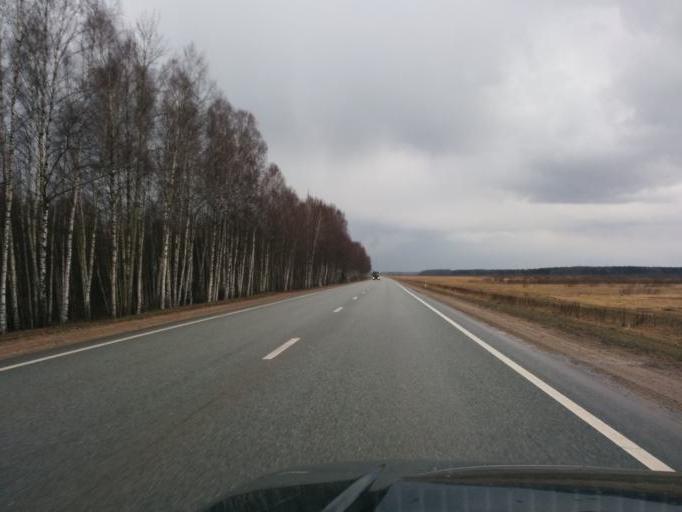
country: LV
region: Marupe
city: Marupe
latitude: 56.8500
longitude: 24.0083
